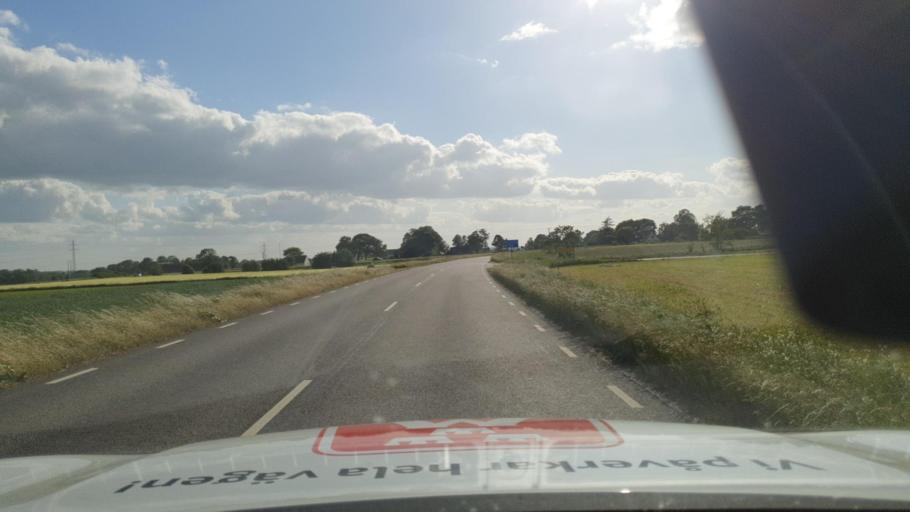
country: SE
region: Skane
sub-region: Tomelilla Kommun
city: Tomelilla
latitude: 55.5642
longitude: 13.9669
